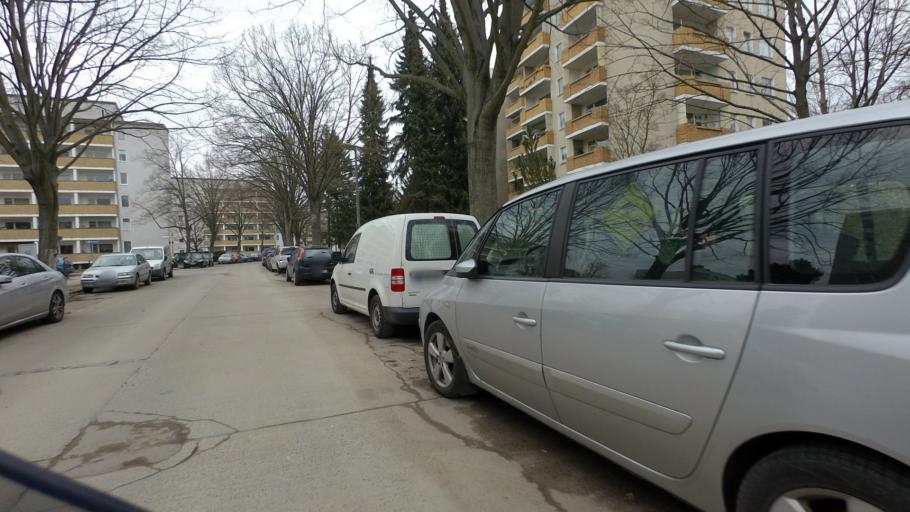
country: DE
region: Berlin
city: Lankwitz
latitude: 52.4310
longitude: 13.3586
